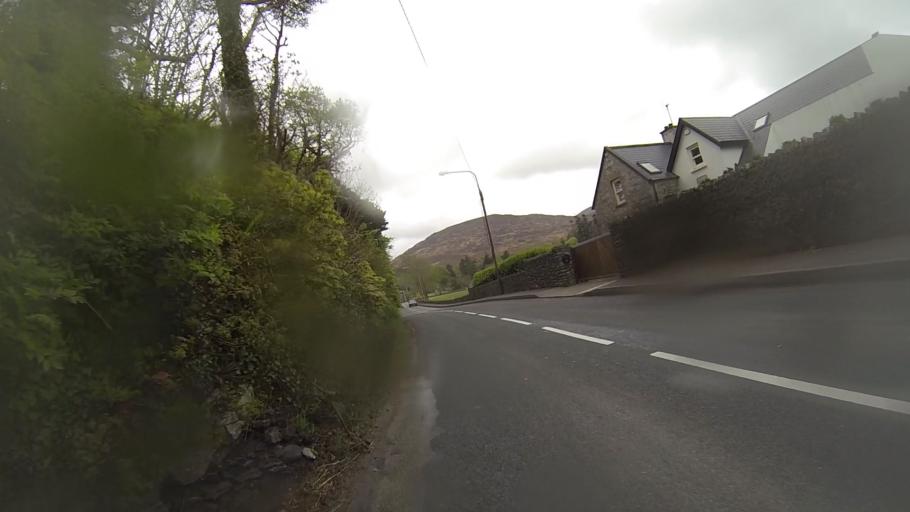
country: IE
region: Munster
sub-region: Ciarrai
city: Kenmare
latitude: 51.8732
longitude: -9.5835
